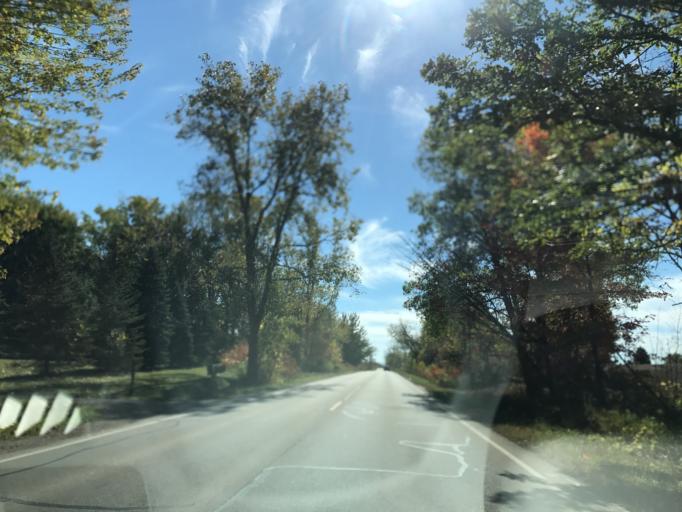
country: US
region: Michigan
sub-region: Oakland County
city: South Lyon
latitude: 42.4086
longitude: -83.6461
